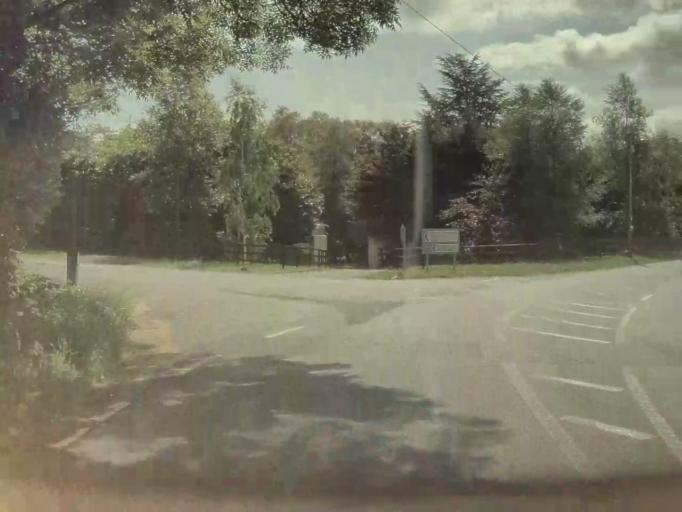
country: IE
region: Leinster
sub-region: Wicklow
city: Rathdrum
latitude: 53.0318
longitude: -6.2496
